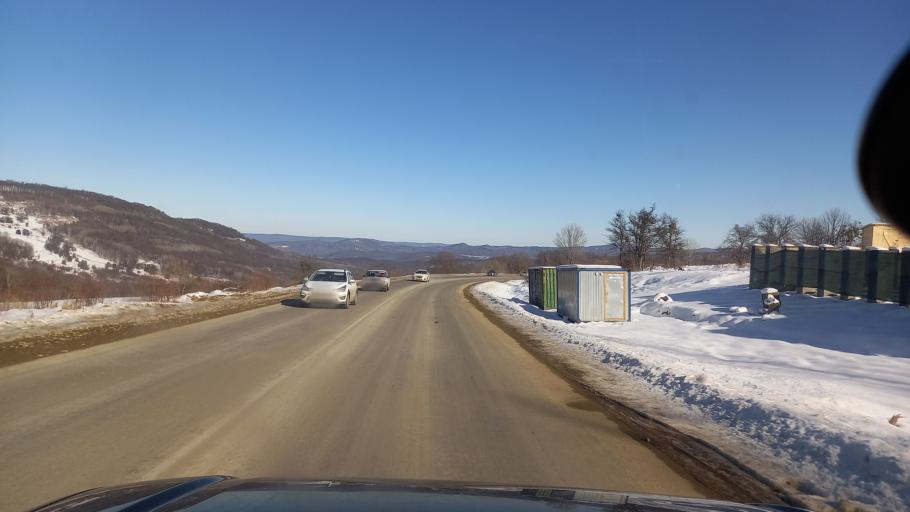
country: RU
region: Adygeya
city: Kamennomostskiy
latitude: 44.2298
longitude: 40.1196
